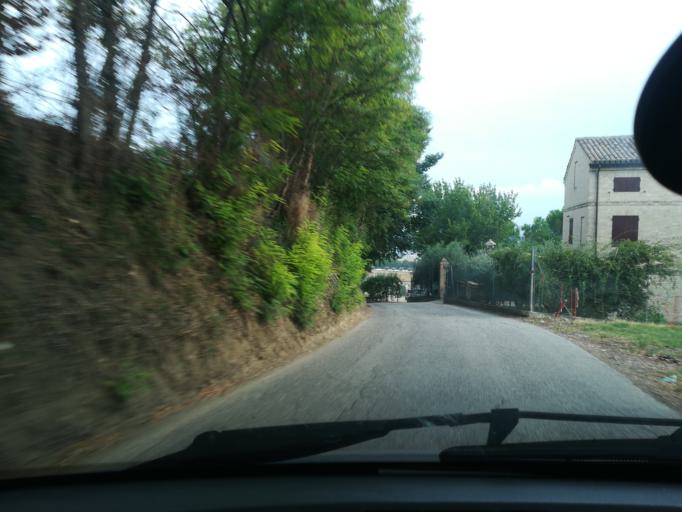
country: IT
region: The Marches
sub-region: Provincia di Macerata
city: Piediripa
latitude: 43.2950
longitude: 13.4846
